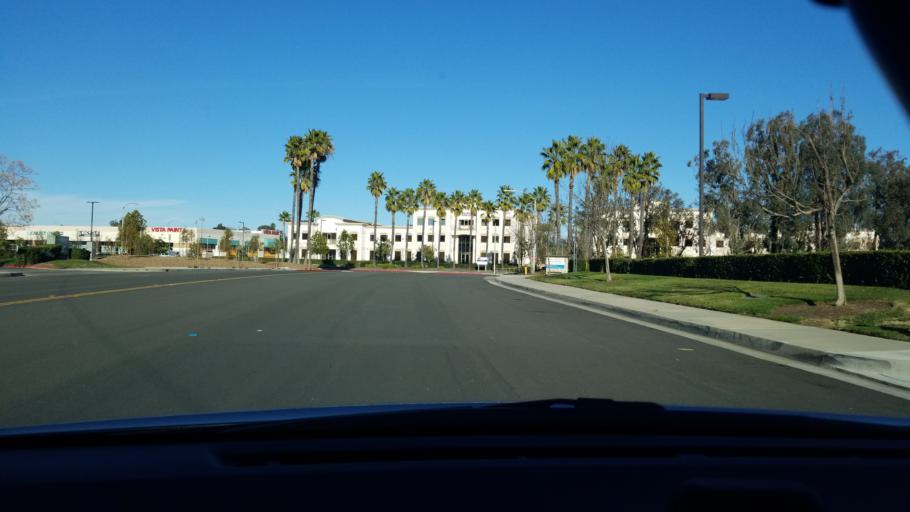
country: US
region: California
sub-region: Riverside County
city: Temecula
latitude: 33.5247
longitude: -117.1677
